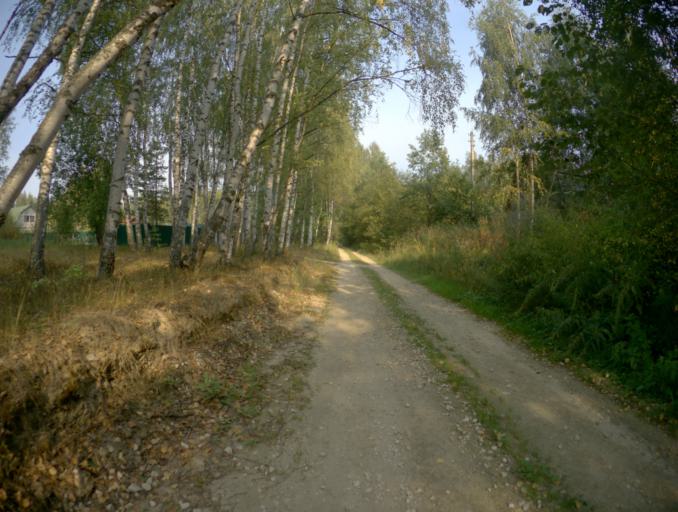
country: RU
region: Vladimir
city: Kosterevo
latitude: 55.9304
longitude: 39.5514
